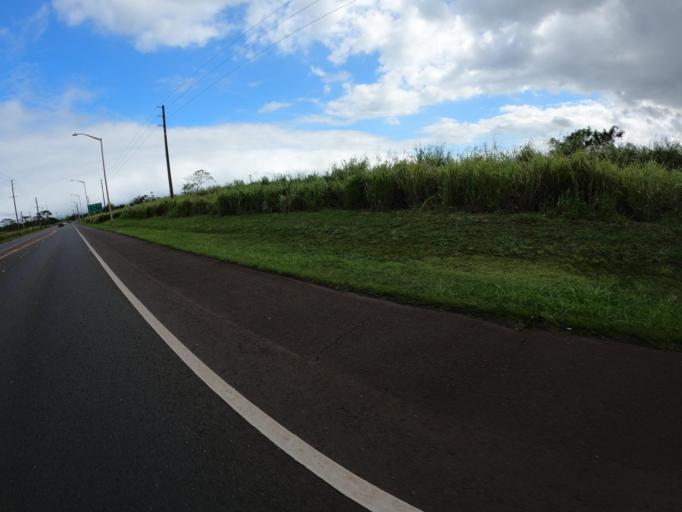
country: US
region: Hawaii
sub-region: Honolulu County
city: Wahiawa
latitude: 21.5068
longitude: -158.0316
